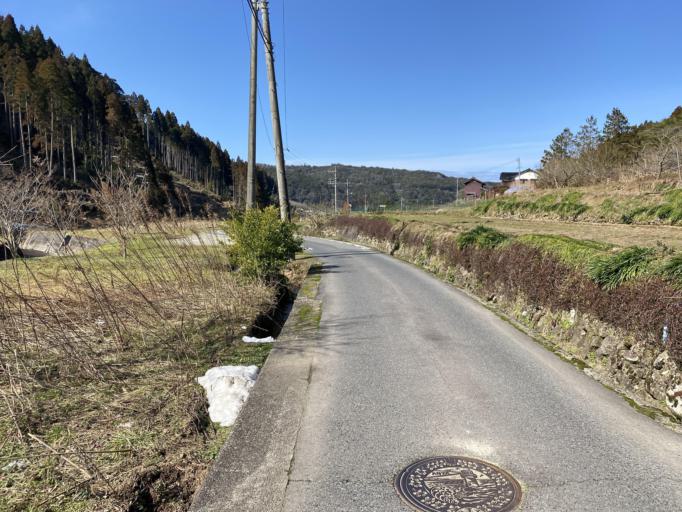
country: JP
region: Tottori
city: Kurayoshi
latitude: 35.4913
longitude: 133.9895
